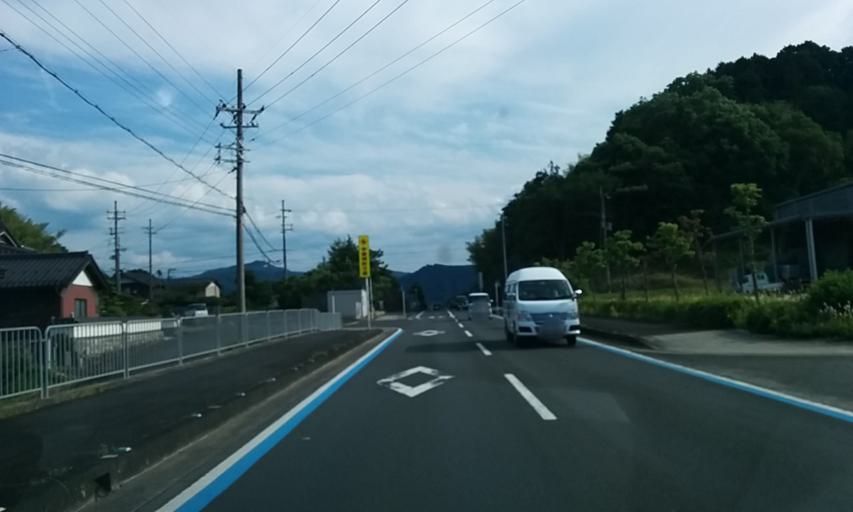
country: JP
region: Kyoto
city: Ayabe
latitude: 35.3173
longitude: 135.2607
